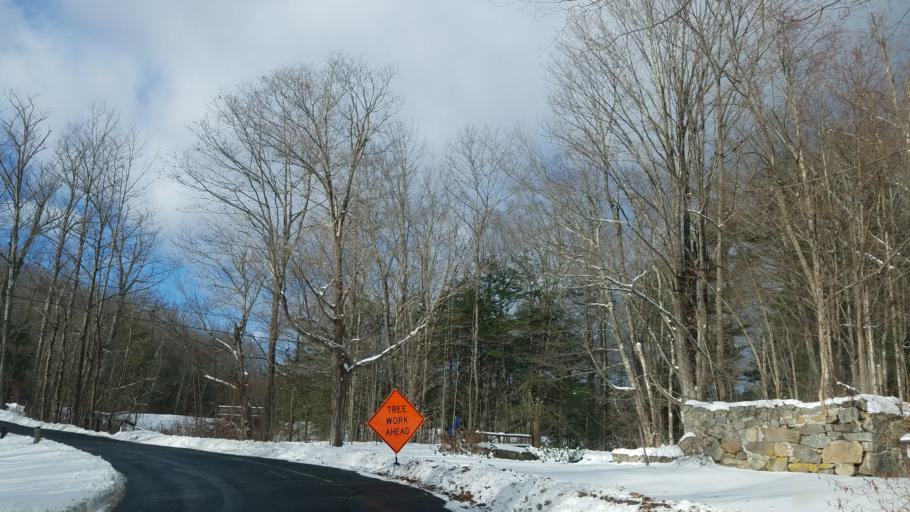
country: US
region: Connecticut
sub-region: Litchfield County
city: Winsted
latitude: 41.9679
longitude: -73.0587
